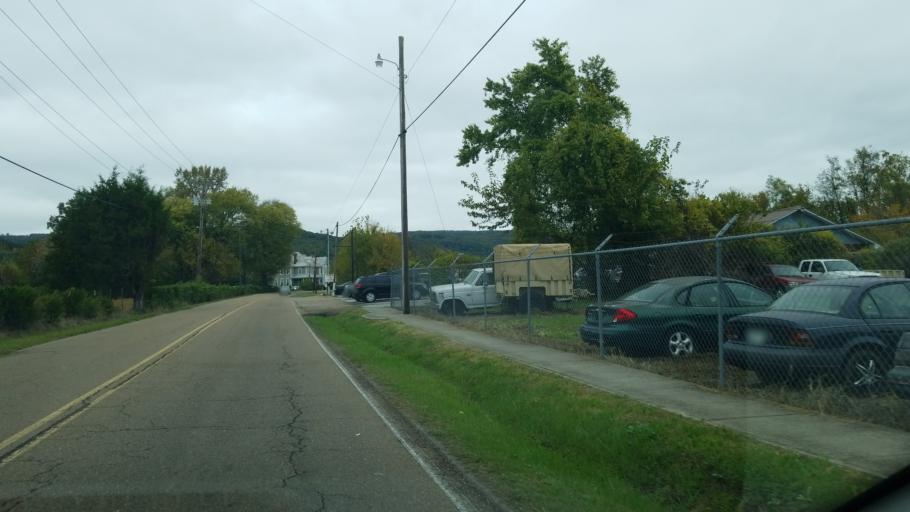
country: US
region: Tennessee
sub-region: Rhea County
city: Dayton
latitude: 35.4907
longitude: -85.0222
